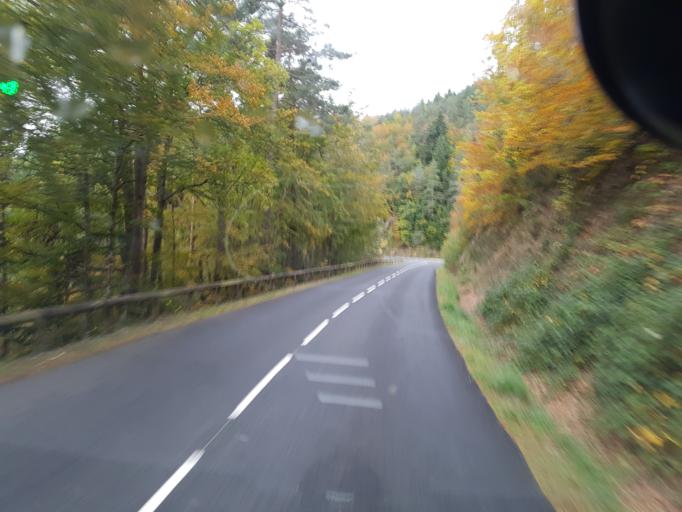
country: FR
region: Auvergne
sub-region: Departement de la Haute-Loire
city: Lapte
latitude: 45.2144
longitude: 4.2061
